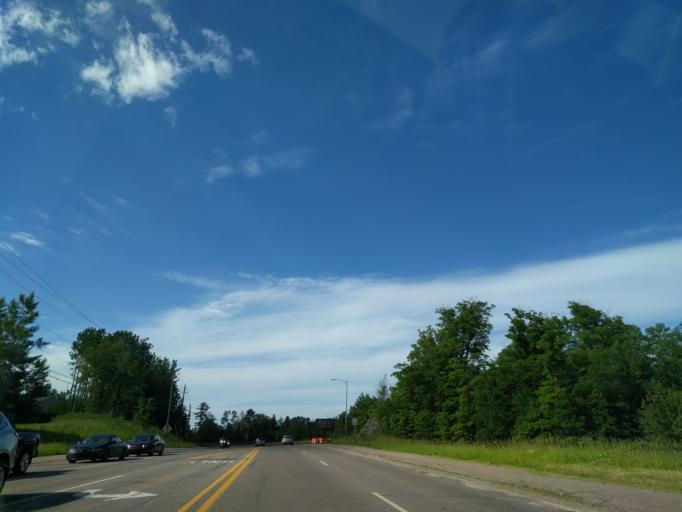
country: US
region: Michigan
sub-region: Marquette County
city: Marquette
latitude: 46.5366
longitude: -87.4171
